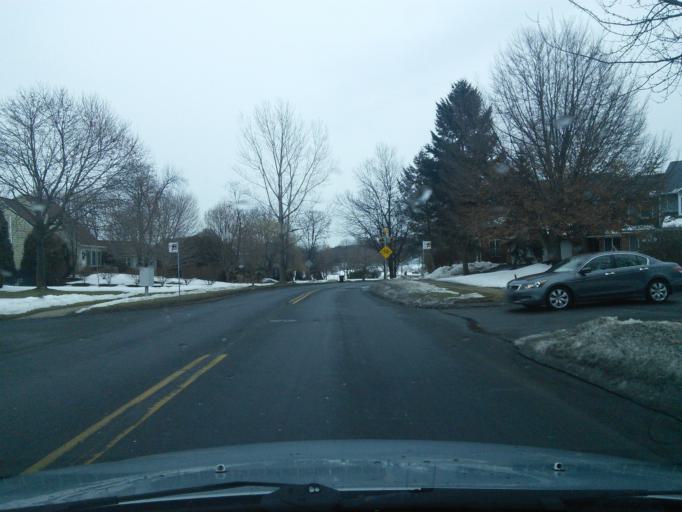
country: US
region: Pennsylvania
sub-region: Centre County
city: State College
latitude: 40.7721
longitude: -77.8679
